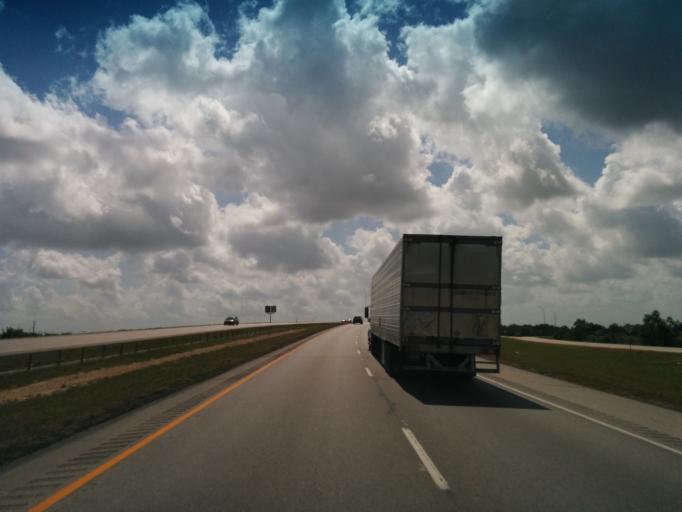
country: US
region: Texas
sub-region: Austin County
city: Sealy
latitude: 29.7637
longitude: -96.1891
